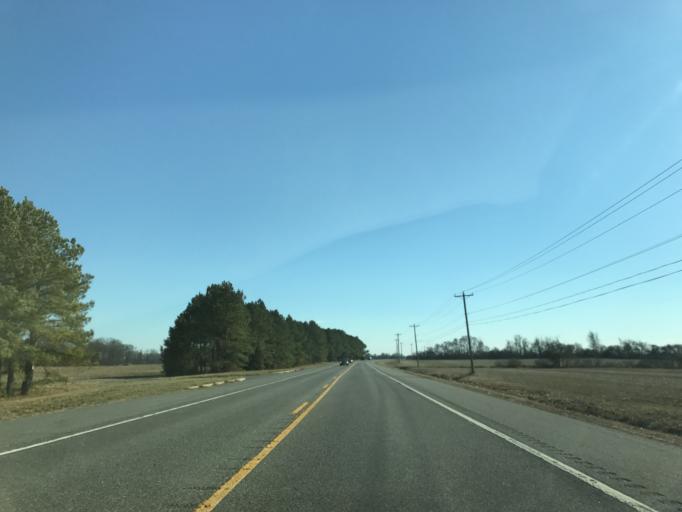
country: US
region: Maryland
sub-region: Queen Anne's County
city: Centreville
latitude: 38.9809
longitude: -76.0706
